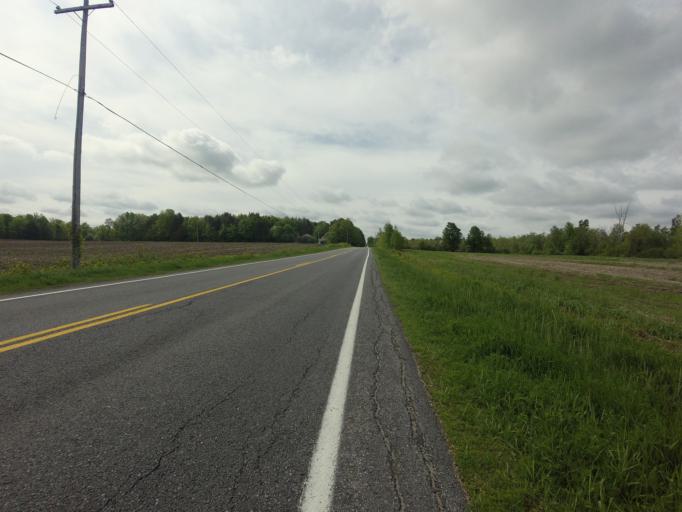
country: CA
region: Ontario
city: Cornwall
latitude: 44.7478
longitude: -74.6677
